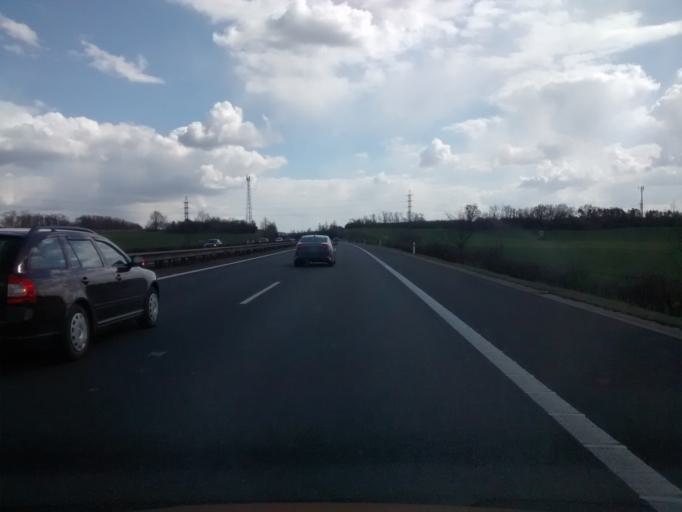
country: CZ
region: Central Bohemia
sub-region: Okres Melnik
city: Veltrusy
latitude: 50.2747
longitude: 14.3561
